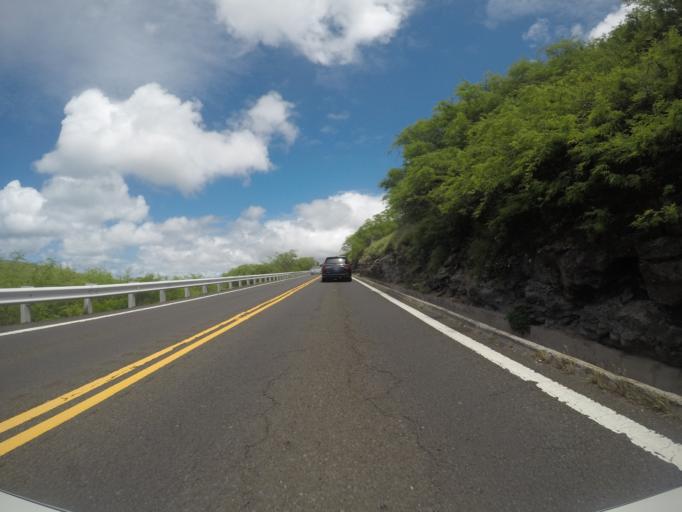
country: US
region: Hawaii
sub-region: Honolulu County
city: Waimanalo Beach
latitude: 21.2734
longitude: -157.6897
